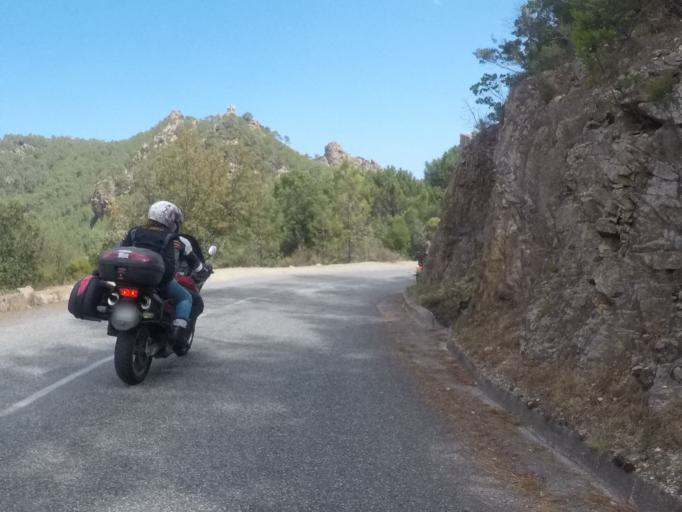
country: FR
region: Corsica
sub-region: Departement de la Corse-du-Sud
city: Sari-Solenzara
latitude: 41.8429
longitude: 9.2997
